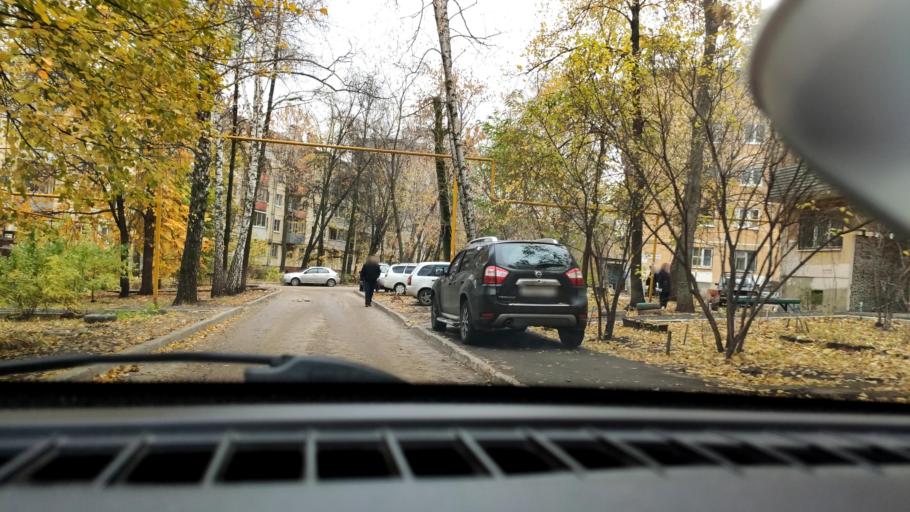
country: RU
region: Samara
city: Samara
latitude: 53.2312
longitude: 50.2183
